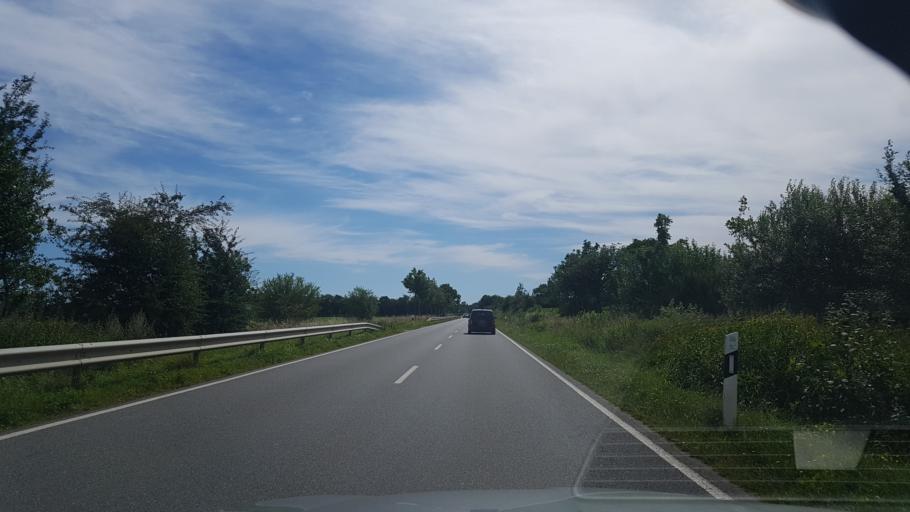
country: DE
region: Schleswig-Holstein
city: Handewitt
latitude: 54.7973
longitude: 9.2844
